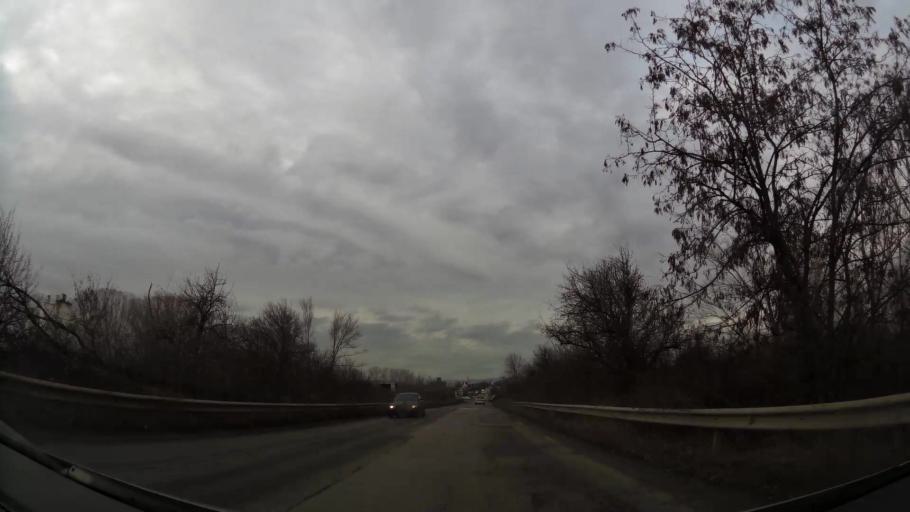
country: BG
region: Sofia-Capital
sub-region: Stolichna Obshtina
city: Sofia
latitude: 42.7505
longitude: 23.2763
